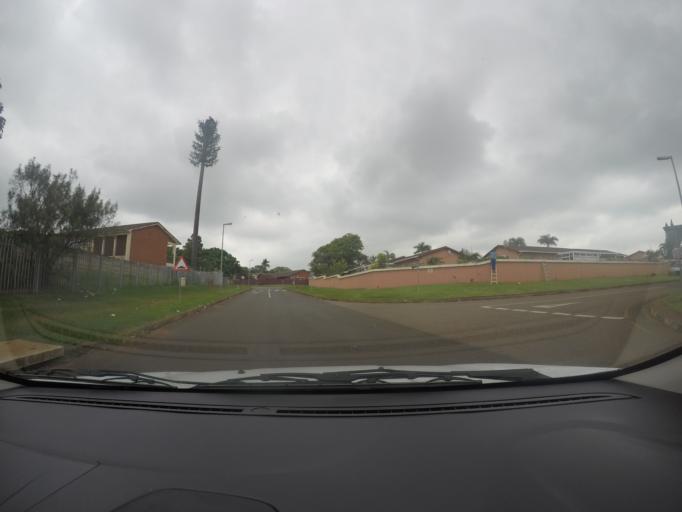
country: ZA
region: KwaZulu-Natal
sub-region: uThungulu District Municipality
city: Empangeni
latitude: -28.7676
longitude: 31.8978
